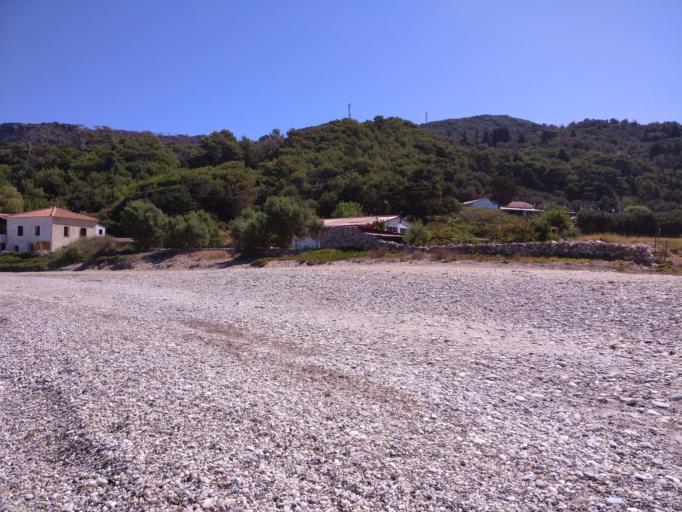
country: GR
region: North Aegean
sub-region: Nomos Samou
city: Neon Karlovasion
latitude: 37.7906
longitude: 26.6654
